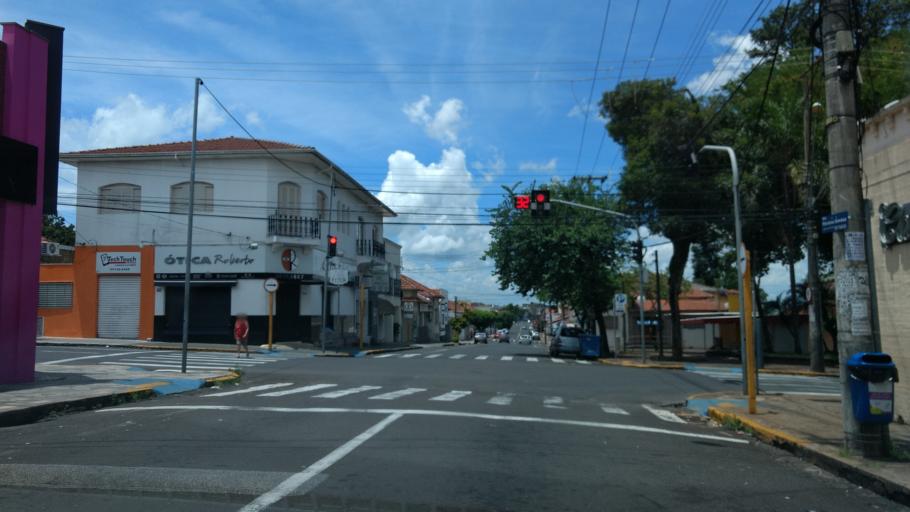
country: BR
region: Sao Paulo
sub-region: Botucatu
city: Botucatu
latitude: -22.8713
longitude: -48.4484
